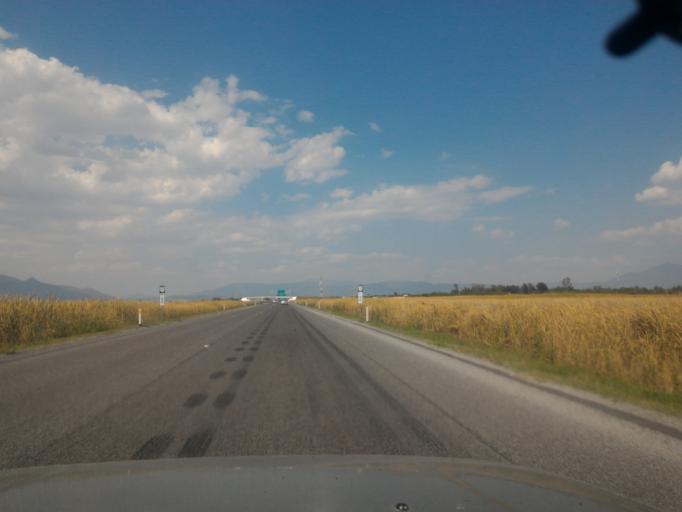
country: MX
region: Jalisco
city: Atoyac
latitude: 20.0065
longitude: -103.5340
